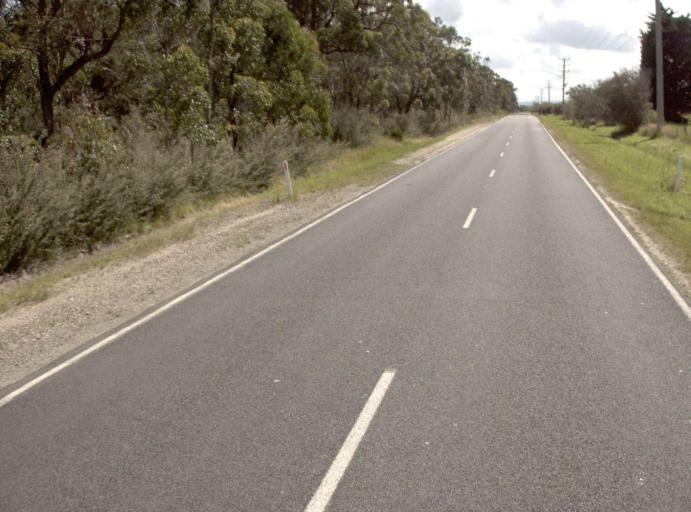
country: AU
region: Victoria
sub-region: Latrobe
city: Traralgon
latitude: -38.1338
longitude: 146.5494
